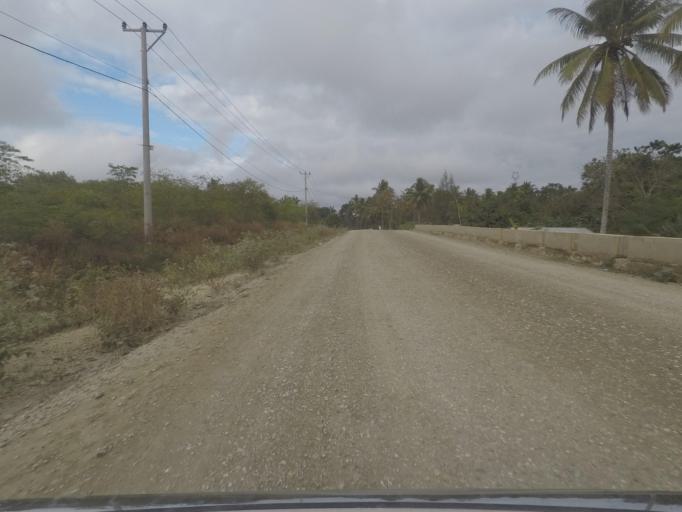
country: TL
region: Baucau
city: Baucau
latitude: -8.4987
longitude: 126.4516
